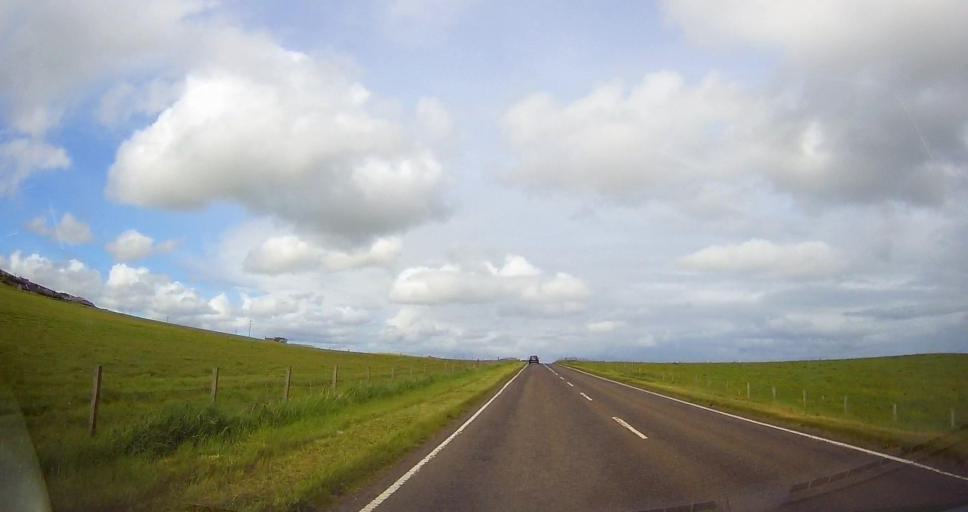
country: GB
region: Scotland
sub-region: Orkney Islands
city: Orkney
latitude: 59.0176
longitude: -3.1040
